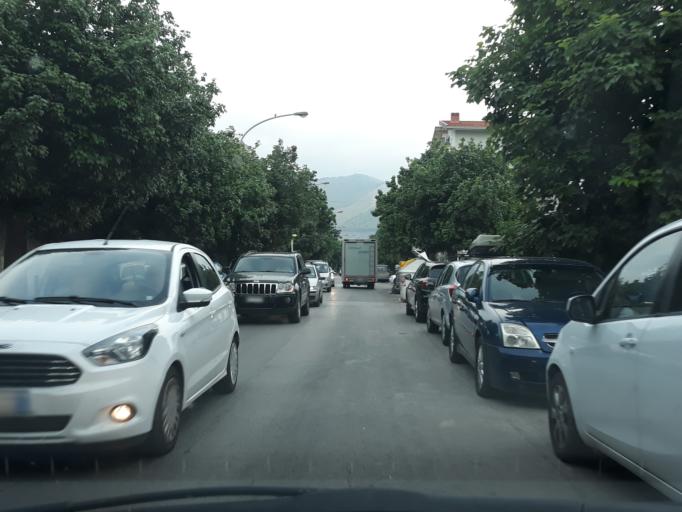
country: IT
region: Sicily
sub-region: Palermo
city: Monreale
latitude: 38.0944
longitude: 13.3195
